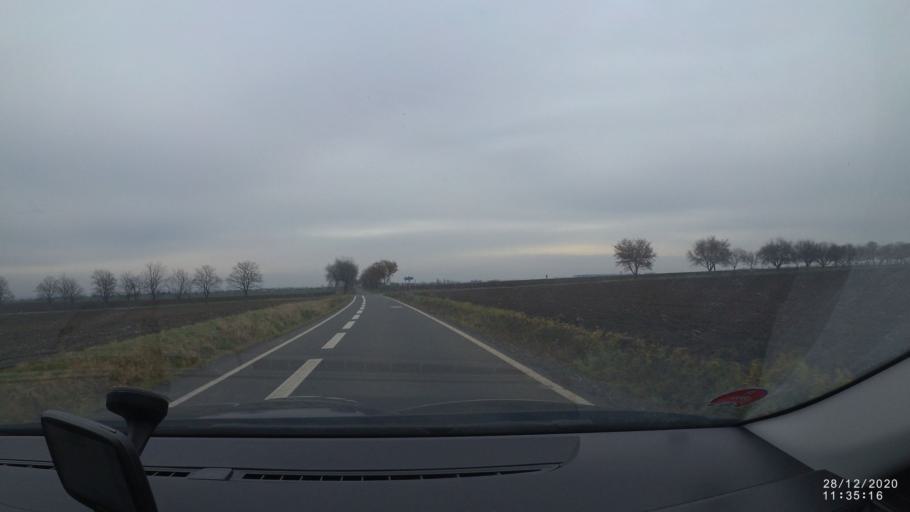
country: CZ
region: Praha
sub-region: Praha 19
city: Satalice
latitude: 50.1321
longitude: 14.5953
